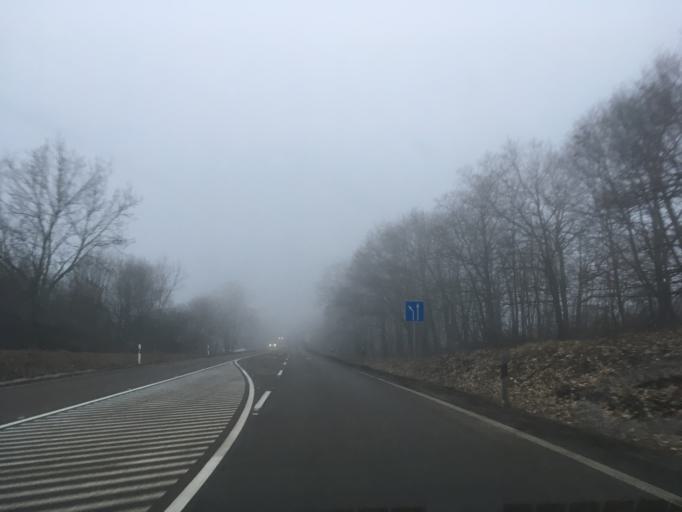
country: HU
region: Heves
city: Egerszalok
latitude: 47.8601
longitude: 20.3723
